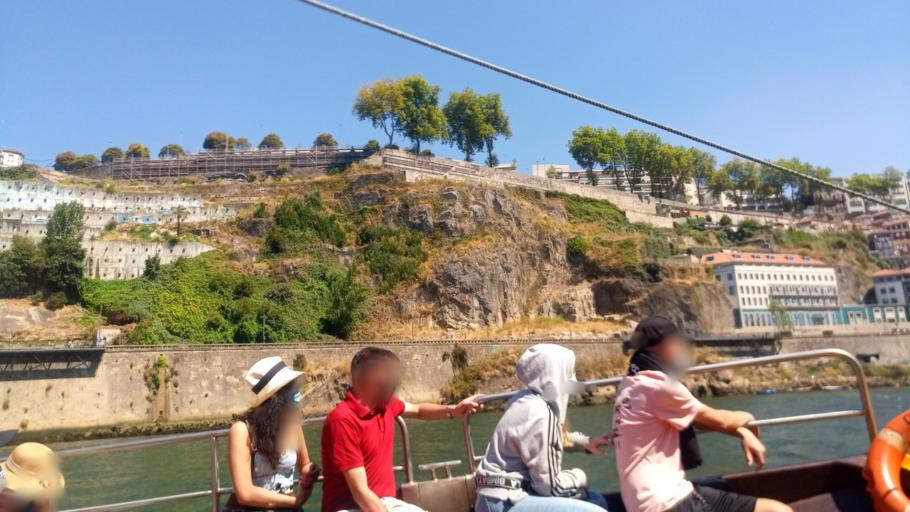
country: PT
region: Porto
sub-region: Porto
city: Porto
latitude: 41.1404
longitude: -8.6065
